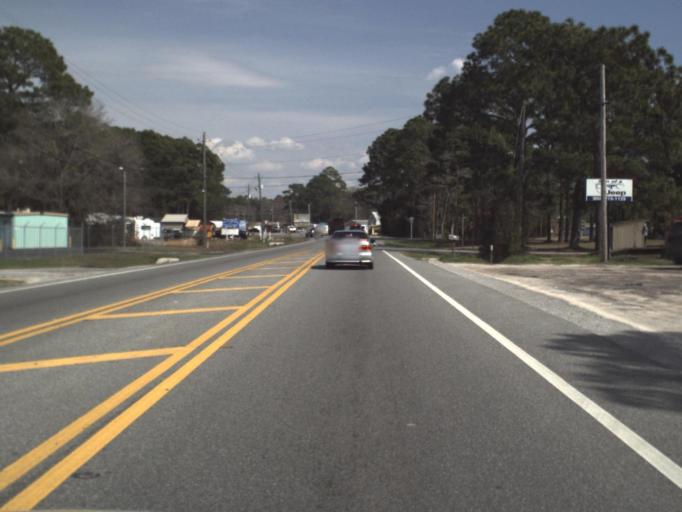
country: US
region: Florida
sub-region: Bay County
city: Pretty Bayou
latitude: 30.1967
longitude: -85.6862
